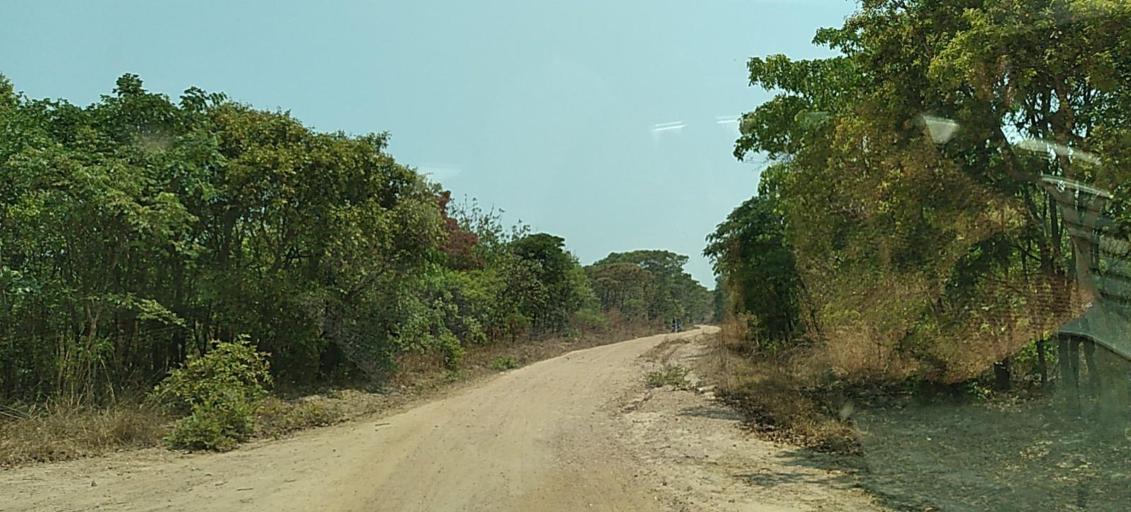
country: ZM
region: Copperbelt
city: Kalulushi
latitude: -12.9492
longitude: 28.1503
